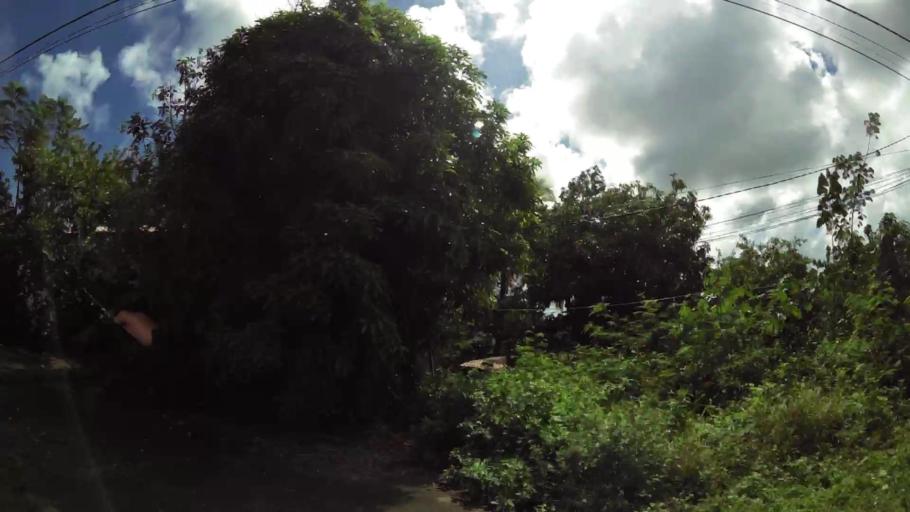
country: GP
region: Guadeloupe
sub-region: Guadeloupe
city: Anse-Bertrand
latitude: 16.4660
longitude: -61.5039
